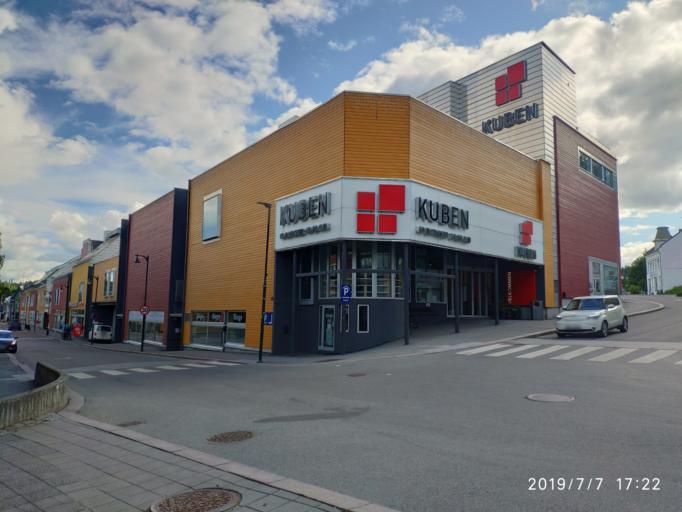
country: NO
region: Buskerud
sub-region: Ringerike
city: Honefoss
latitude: 60.1658
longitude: 10.2544
